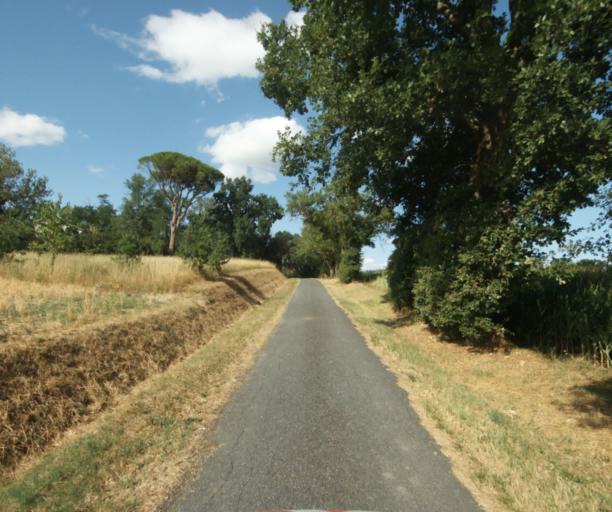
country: FR
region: Midi-Pyrenees
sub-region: Departement du Tarn
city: Puylaurens
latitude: 43.5256
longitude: 1.9866
